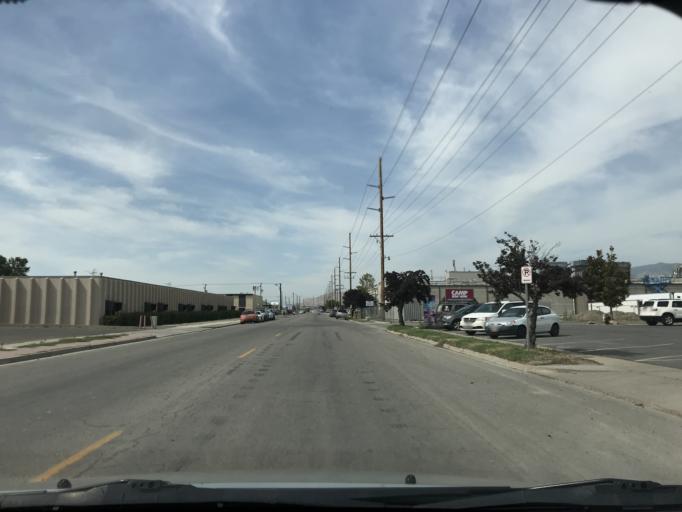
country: US
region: Utah
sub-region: Salt Lake County
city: Centerfield
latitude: 40.6930
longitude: -111.9055
